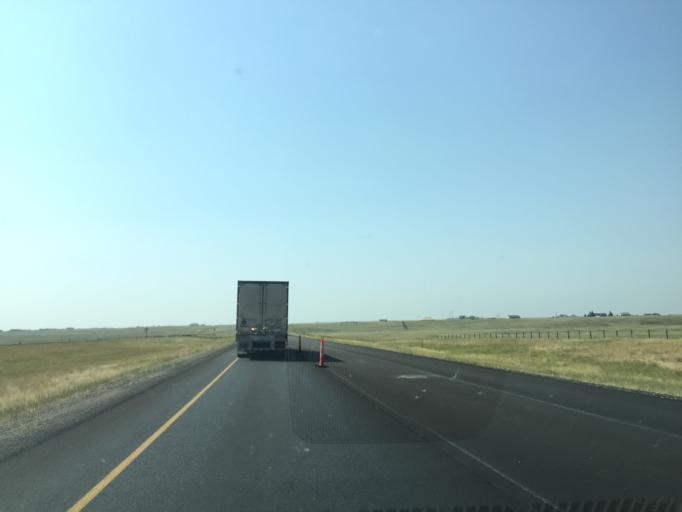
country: US
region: Wyoming
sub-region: Laramie County
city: Ranchettes
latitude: 41.3136
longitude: -104.8587
